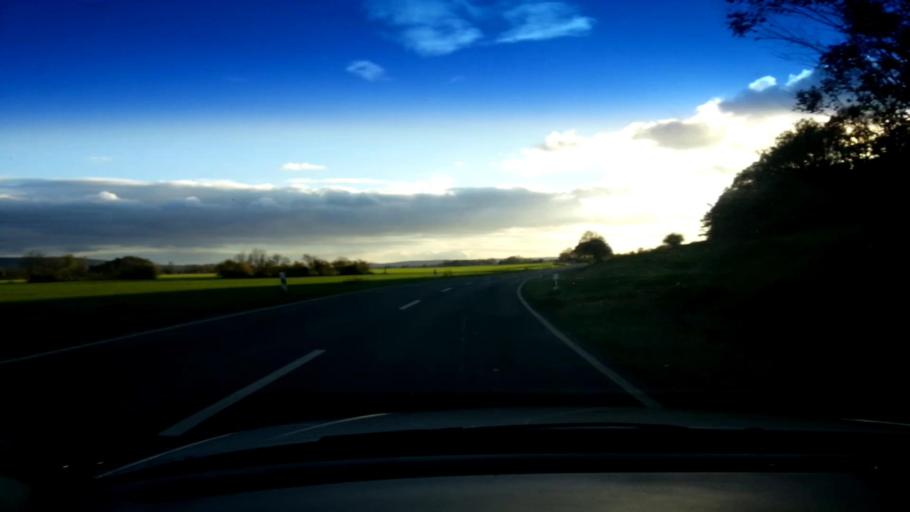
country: DE
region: Bavaria
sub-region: Upper Franconia
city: Zapfendorf
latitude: 50.0440
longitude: 10.9241
